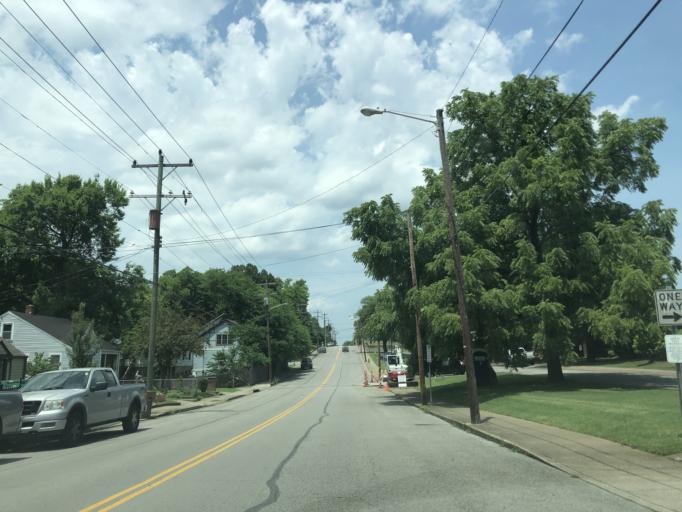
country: US
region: Tennessee
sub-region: Davidson County
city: Nashville
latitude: 36.1791
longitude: -86.7552
